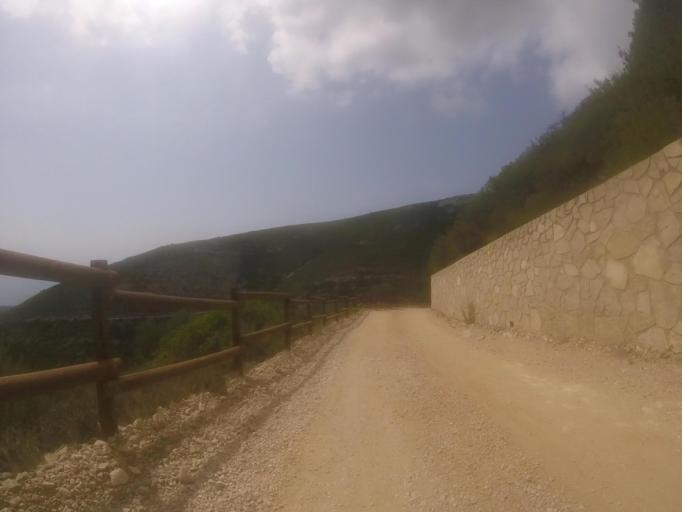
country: ES
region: Valencia
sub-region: Provincia de Castello
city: Peniscola
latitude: 40.3469
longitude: 0.3566
